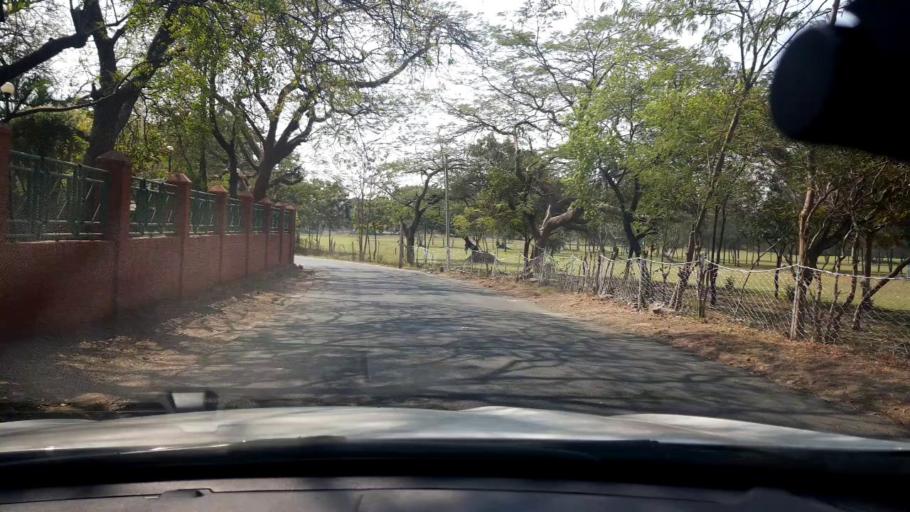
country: IN
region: Maharashtra
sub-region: Pune Division
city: Khadki
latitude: 18.5471
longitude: 73.8595
